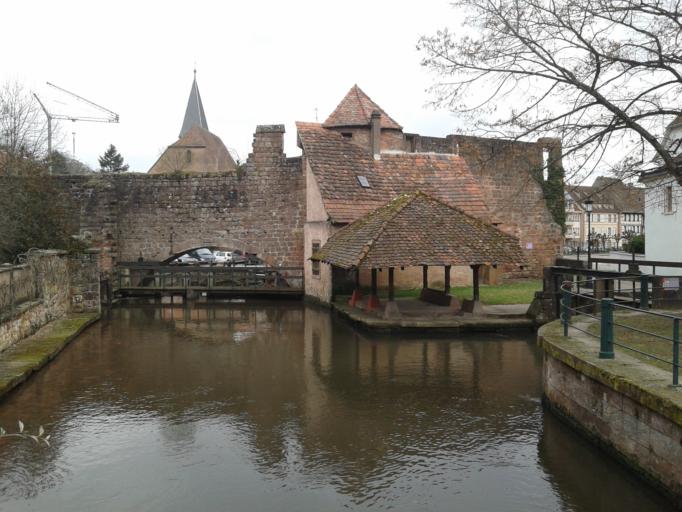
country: FR
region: Alsace
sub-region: Departement du Bas-Rhin
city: Wissembourg
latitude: 49.0384
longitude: 7.9408
